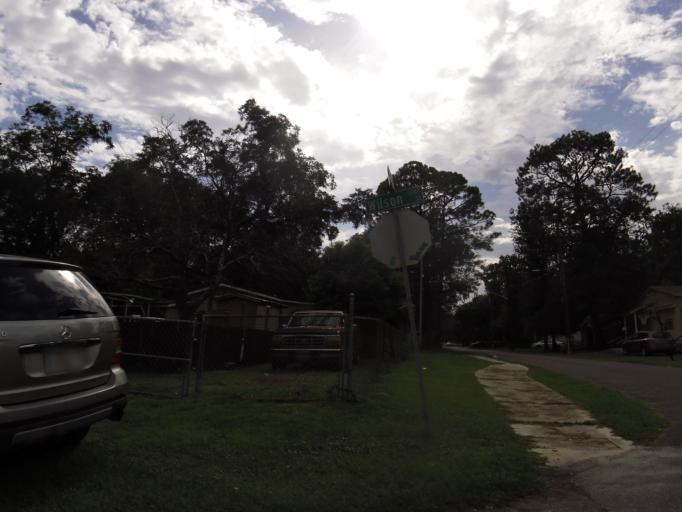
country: US
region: Florida
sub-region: Duval County
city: Jacksonville
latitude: 30.3615
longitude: -81.6813
